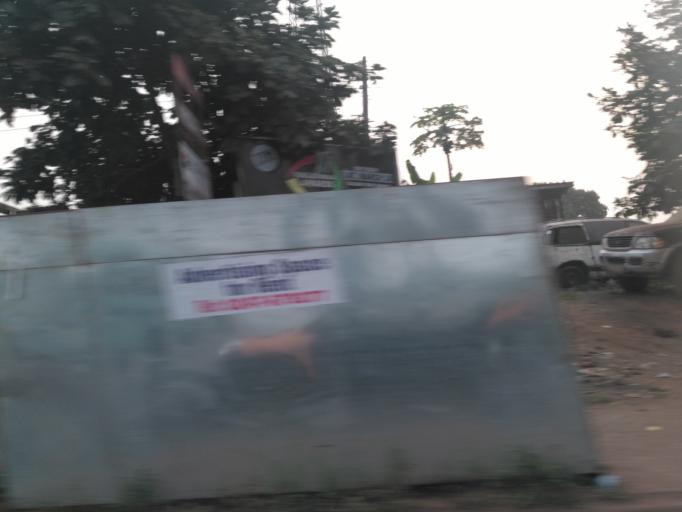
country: GH
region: Ashanti
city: Kumasi
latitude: 6.6799
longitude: -1.6111
